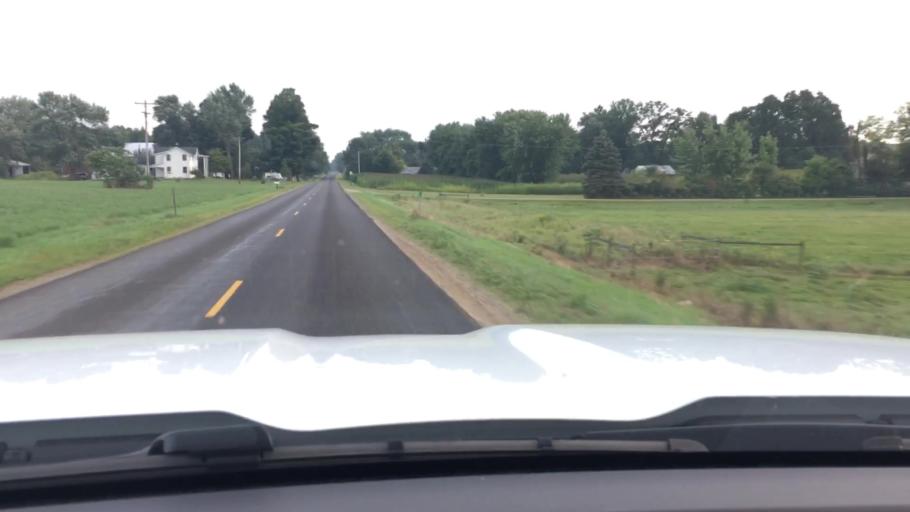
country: US
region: Michigan
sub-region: Ottawa County
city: Hudsonville
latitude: 42.7998
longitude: -85.8814
